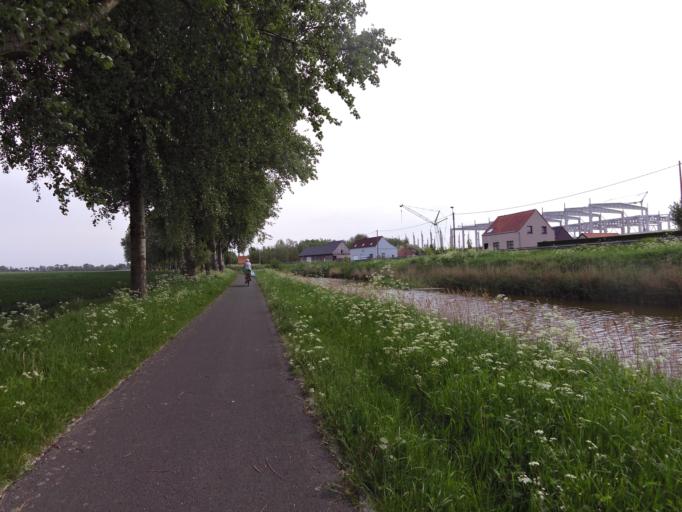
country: BE
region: Flanders
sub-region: Provincie West-Vlaanderen
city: Bredene
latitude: 51.2199
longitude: 2.9961
